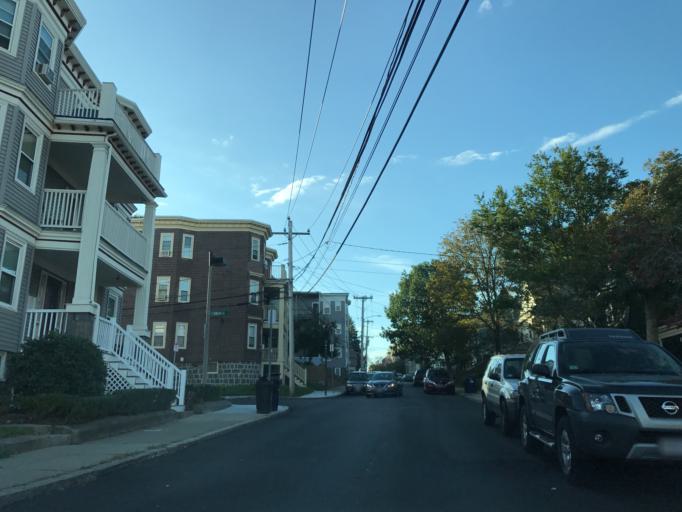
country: US
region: Massachusetts
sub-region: Suffolk County
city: South Boston
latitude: 42.2946
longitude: -71.0550
